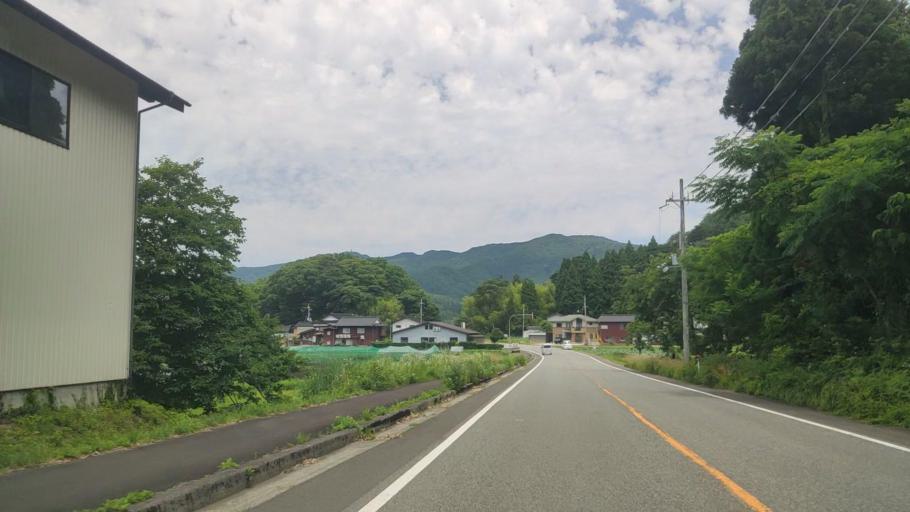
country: JP
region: Hyogo
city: Toyooka
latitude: 35.5008
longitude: 134.6730
